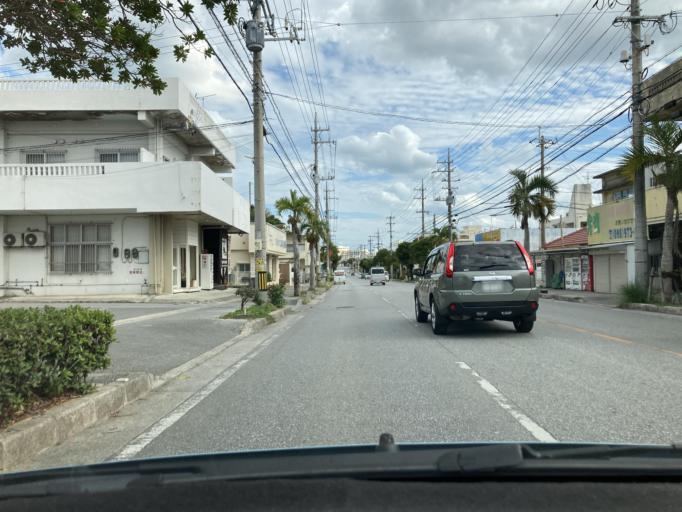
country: JP
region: Okinawa
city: Okinawa
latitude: 26.3578
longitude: 127.8263
